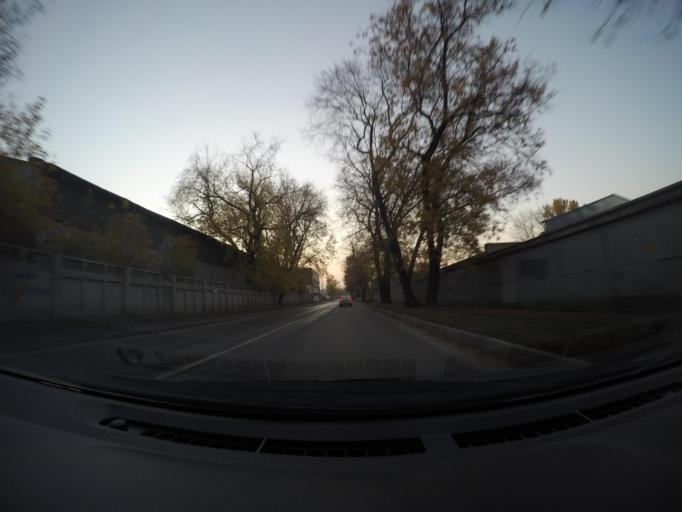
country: RU
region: Moskovskaya
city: Lyubertsy
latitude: 55.6674
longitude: 37.8875
